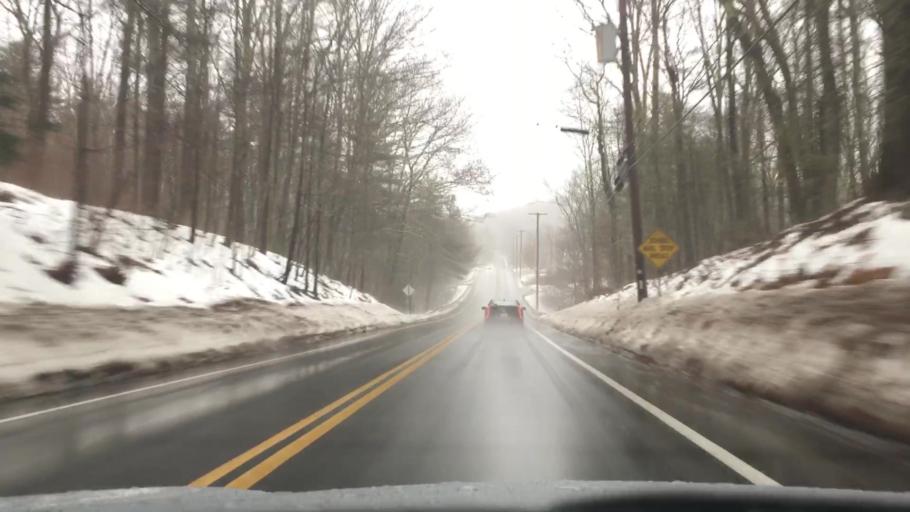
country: US
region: Massachusetts
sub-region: Franklin County
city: Shutesbury
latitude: 42.4886
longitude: -72.3412
